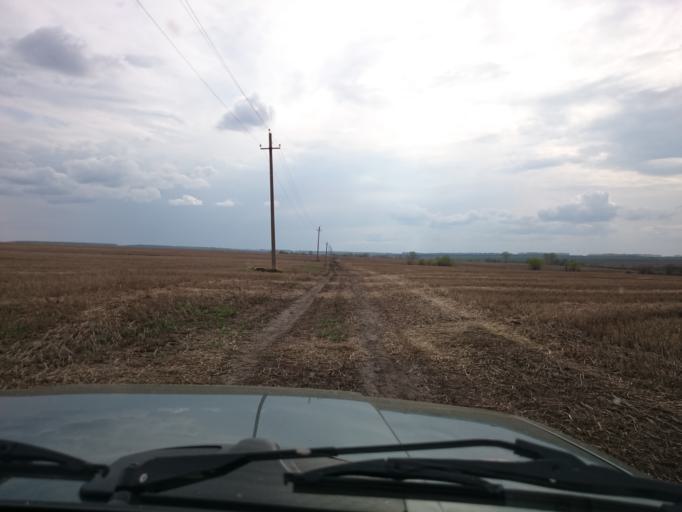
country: RU
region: Mordoviya
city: Kadoshkino
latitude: 54.0219
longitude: 44.4717
